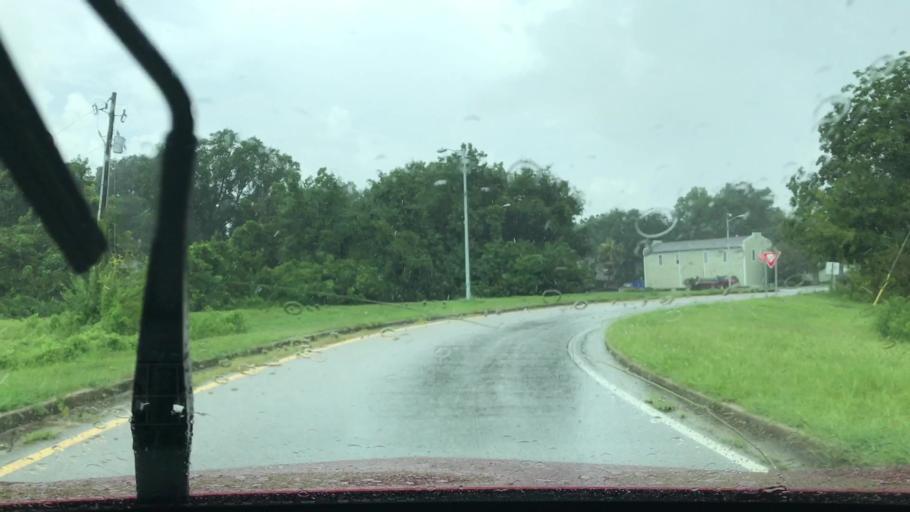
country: US
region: South Carolina
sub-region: Charleston County
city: North Charleston
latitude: 32.8447
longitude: -79.9792
